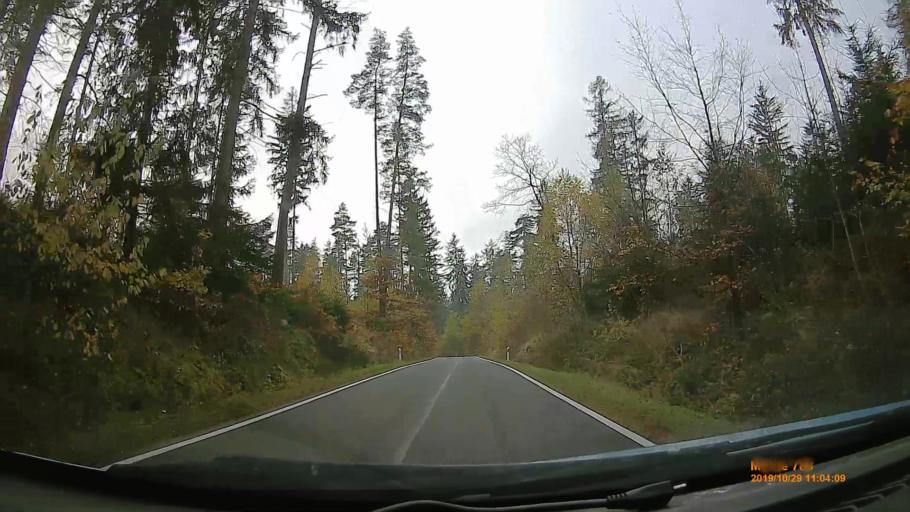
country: PL
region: Lower Silesian Voivodeship
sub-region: Powiat klodzki
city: Szczytna
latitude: 50.4795
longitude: 16.4662
